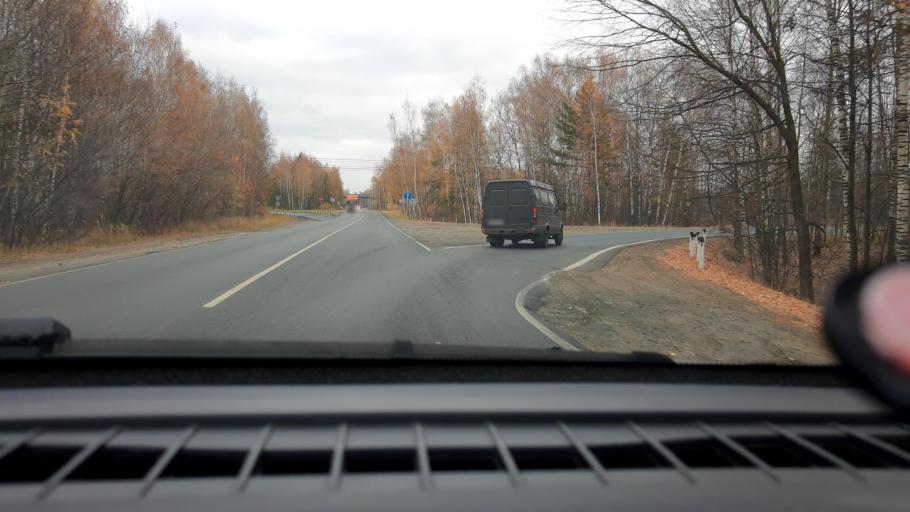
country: RU
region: Nizjnij Novgorod
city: Gorbatovka
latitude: 56.2621
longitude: 43.6988
